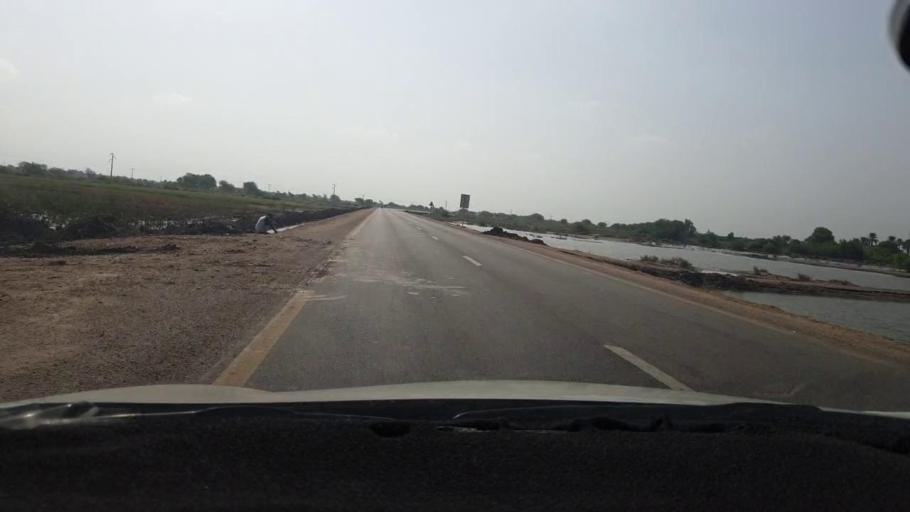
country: PK
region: Sindh
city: Jhol
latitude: 25.8601
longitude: 69.0573
